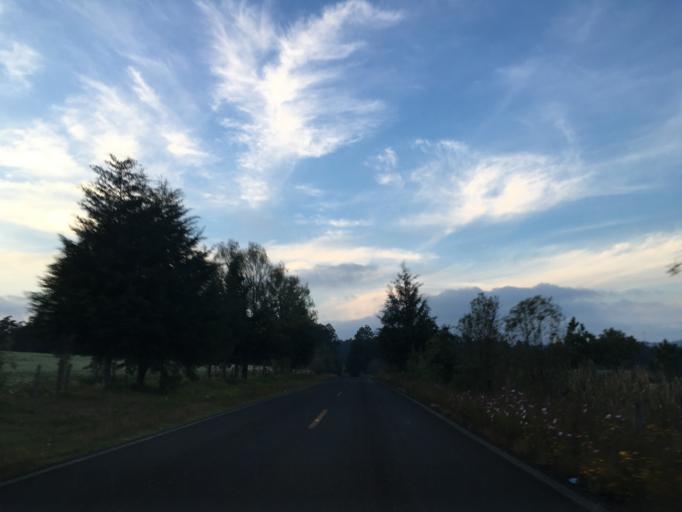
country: MX
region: Michoacan
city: Charapan
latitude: 19.6266
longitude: -102.2429
